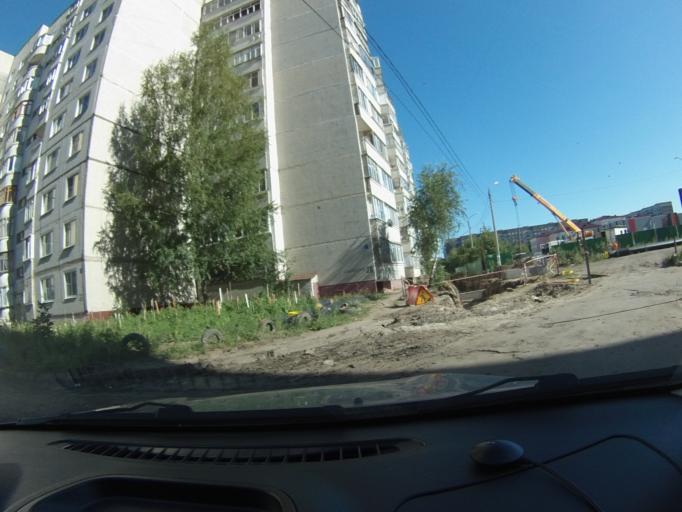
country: RU
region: Tambov
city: Tambov
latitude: 52.7693
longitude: 41.4077
